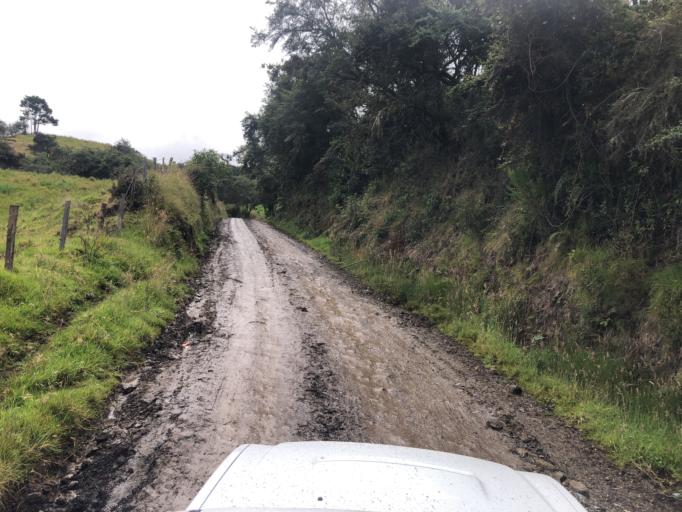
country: CO
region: Cauca
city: Totoro
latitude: 2.4829
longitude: -76.2869
